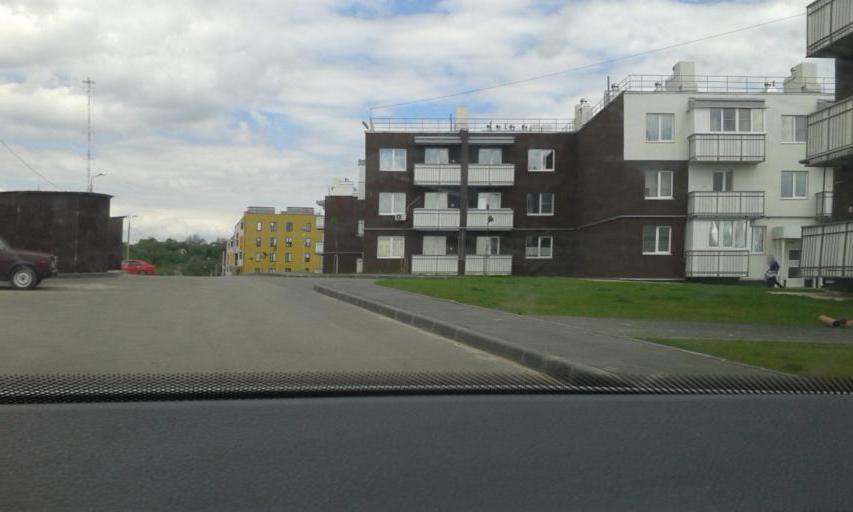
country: RU
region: Volgograd
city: Volgograd
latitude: 48.6627
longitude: 44.4066
